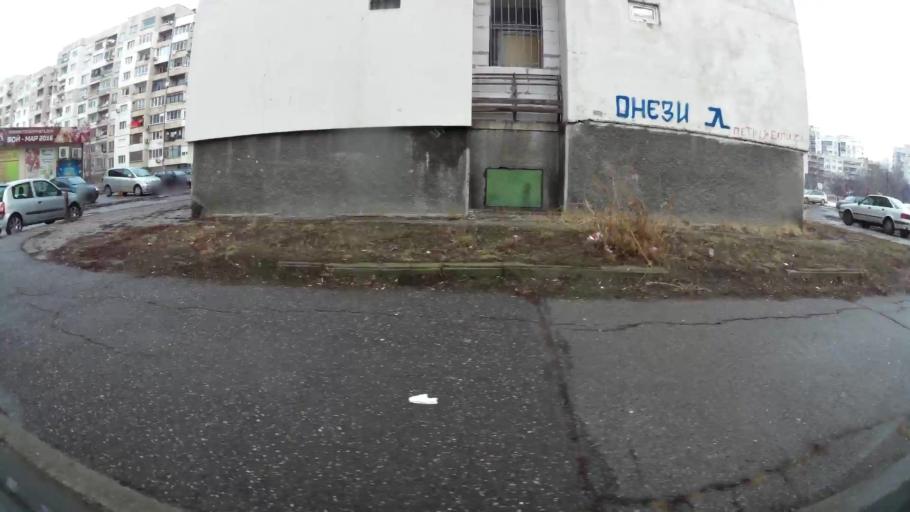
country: BG
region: Sofia-Capital
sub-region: Stolichna Obshtina
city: Sofia
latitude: 42.7107
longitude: 23.2628
